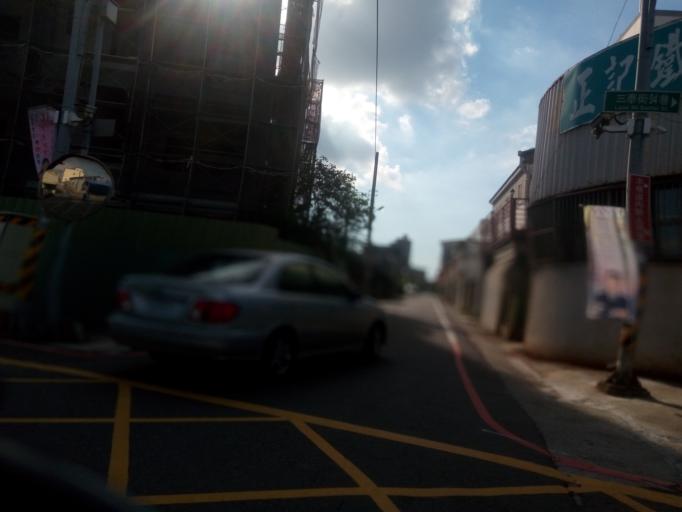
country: TW
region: Taiwan
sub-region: Miaoli
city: Miaoli
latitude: 24.6923
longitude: 120.8781
